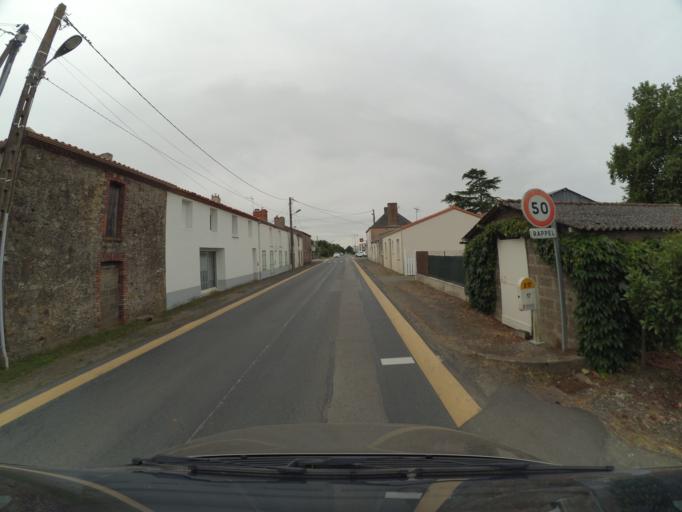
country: FR
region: Pays de la Loire
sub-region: Departement de la Vendee
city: Saint-Andre-Treize-Voies
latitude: 46.9371
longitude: -1.4071
